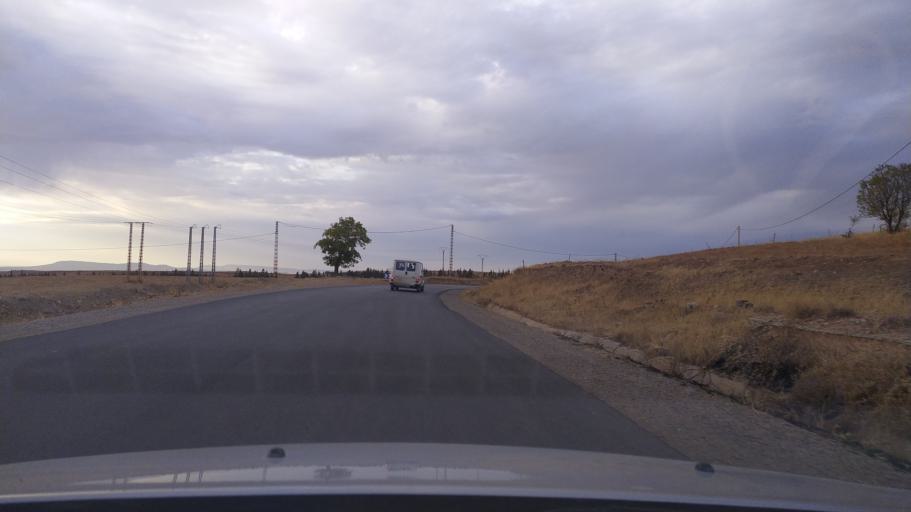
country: DZ
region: Tiaret
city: Frenda
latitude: 35.0222
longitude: 1.1000
